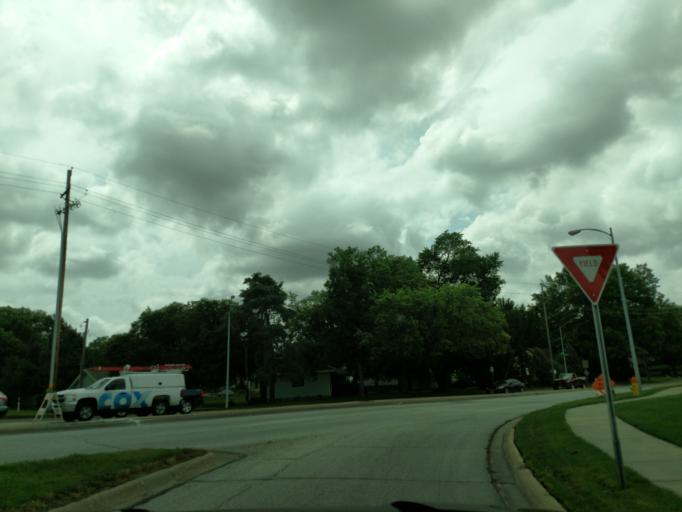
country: US
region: Nebraska
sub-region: Douglas County
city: Ralston
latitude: 41.2123
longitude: -96.0049
